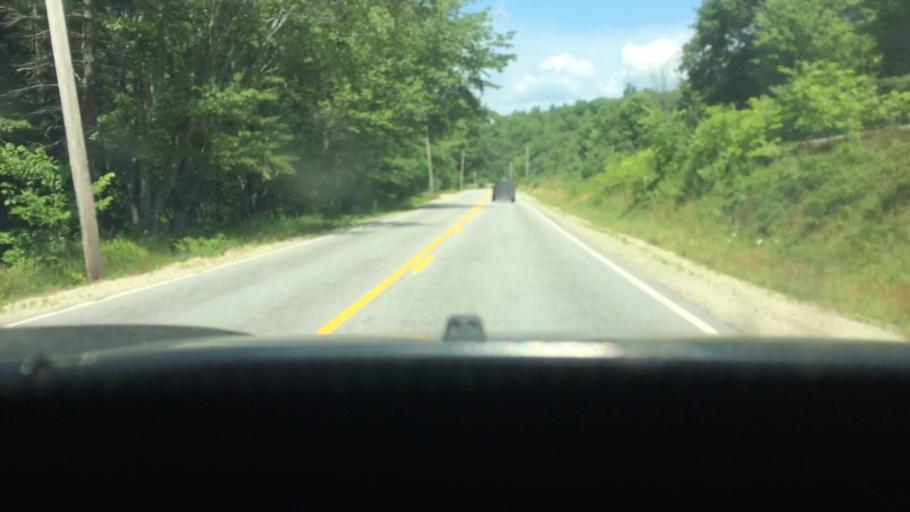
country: US
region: Maine
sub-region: Androscoggin County
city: Mechanic Falls
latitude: 44.1226
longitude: -70.4321
